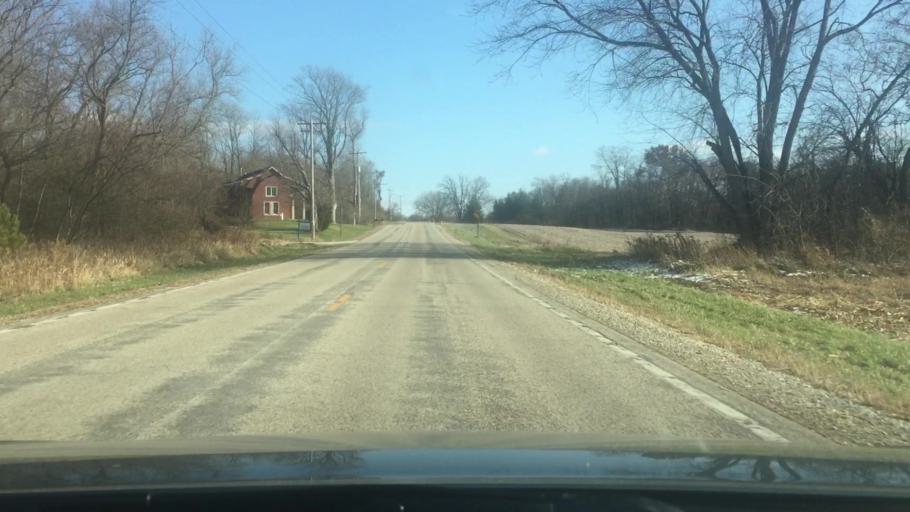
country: US
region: Wisconsin
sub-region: Jefferson County
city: Palmyra
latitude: 42.9352
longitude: -88.5844
